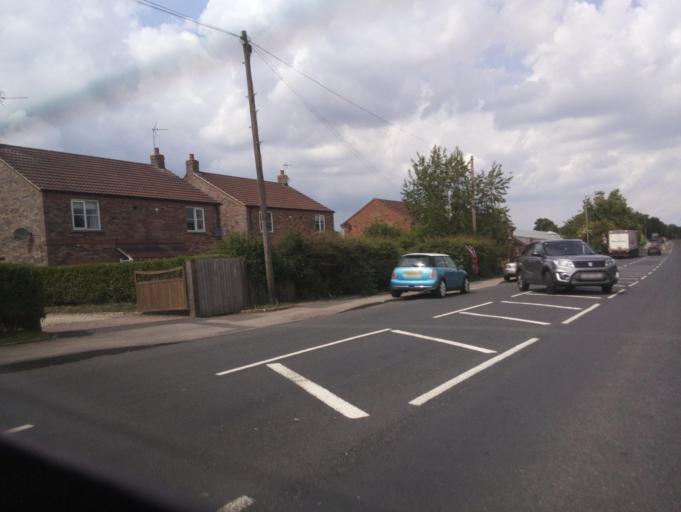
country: GB
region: England
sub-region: North Yorkshire
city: Boroughbridge
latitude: 54.0849
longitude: -1.3959
